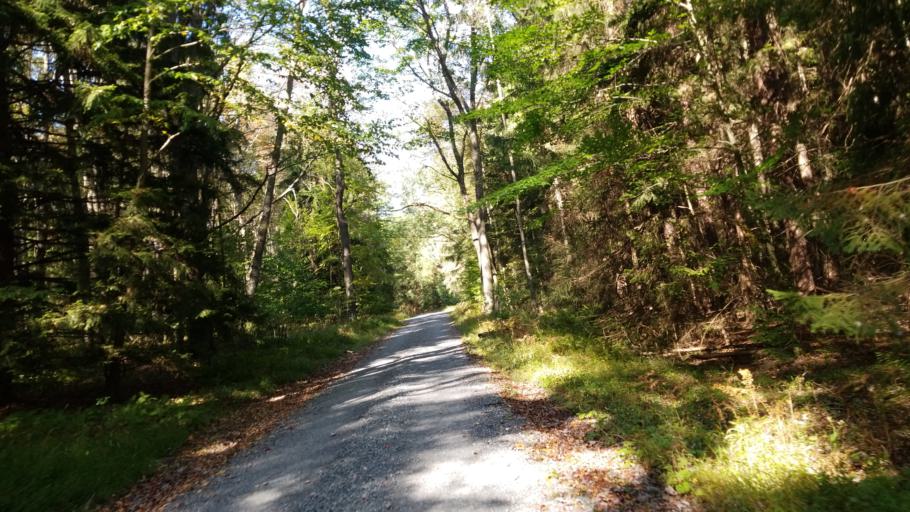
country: US
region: Pennsylvania
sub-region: Clearfield County
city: Clearfield
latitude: 41.1882
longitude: -78.5146
